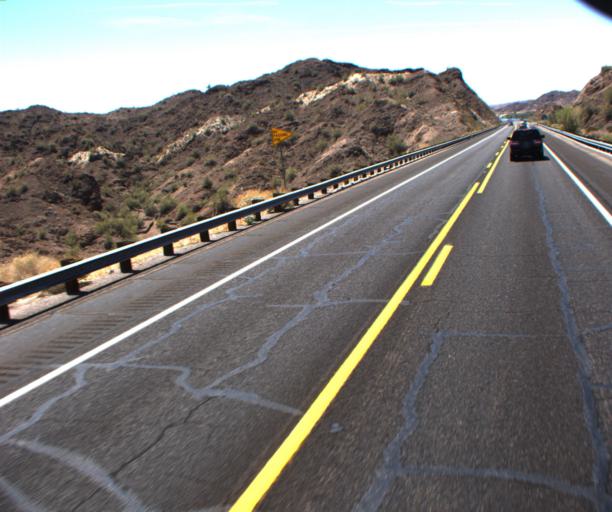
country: US
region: Arizona
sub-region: La Paz County
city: Cienega Springs
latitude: 34.2434
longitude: -114.1683
